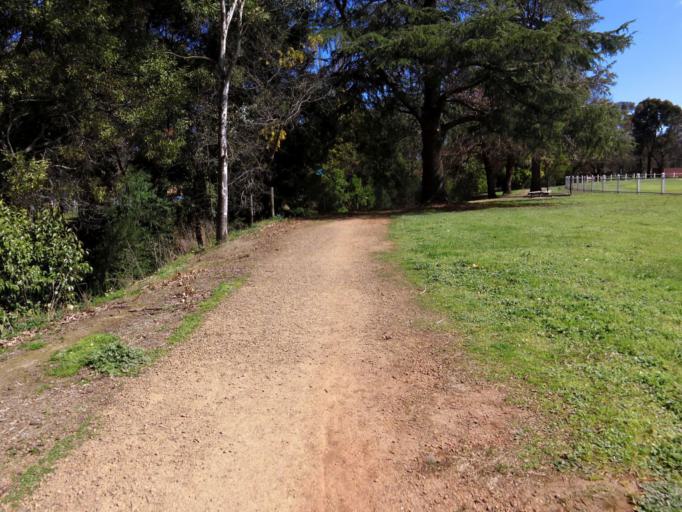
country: AU
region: Victoria
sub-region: Murrindindi
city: Alexandra
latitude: -37.1881
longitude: 145.7137
